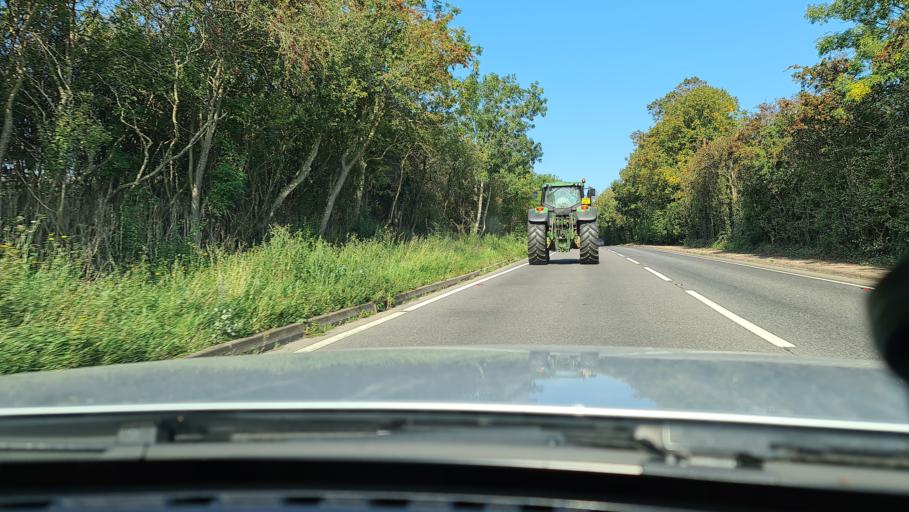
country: GB
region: England
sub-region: Northamptonshire
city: Bugbrooke
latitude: 52.2047
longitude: -1.0453
